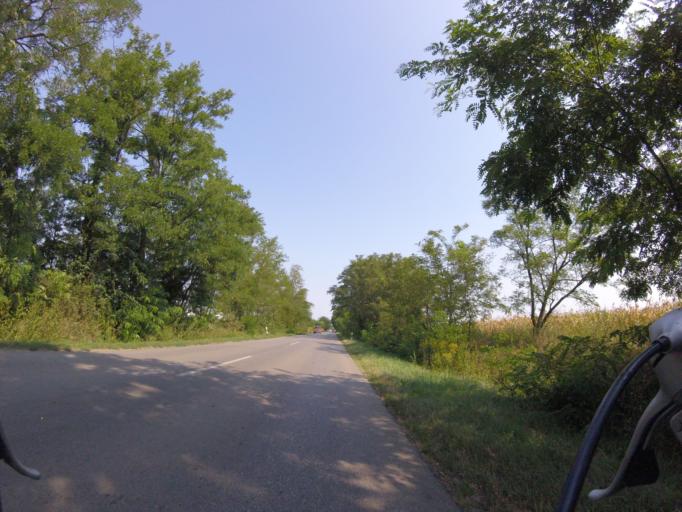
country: HU
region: Szabolcs-Szatmar-Bereg
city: Buj
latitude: 48.0858
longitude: 21.6404
